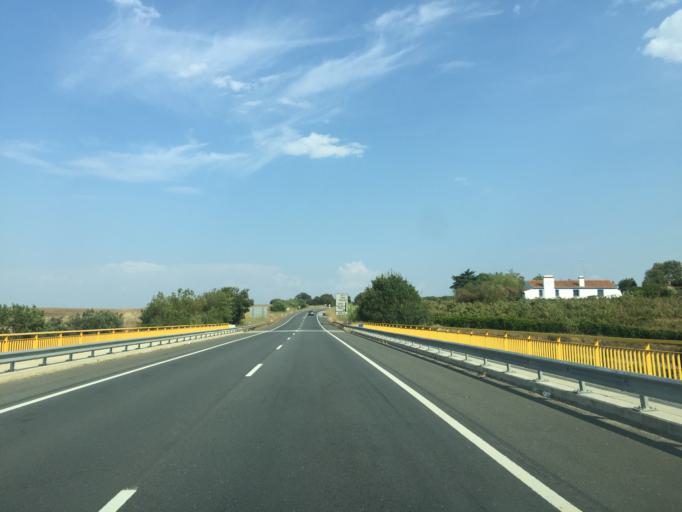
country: PT
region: Setubal
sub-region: Grandola
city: Grandola
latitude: 38.0116
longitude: -8.3847
